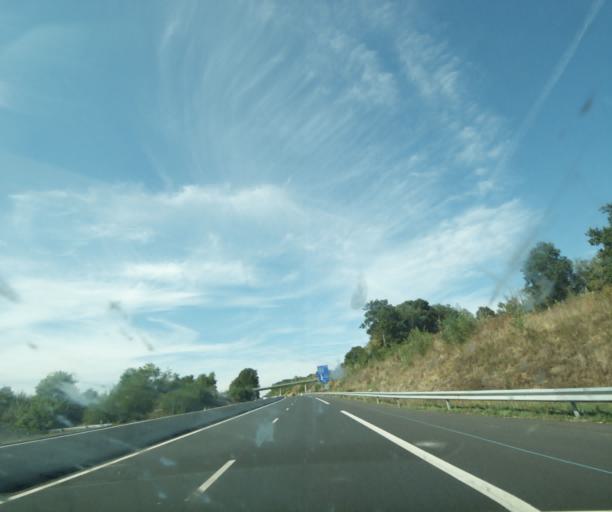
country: FR
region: Limousin
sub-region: Departement de la Correze
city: Saint-Mexant
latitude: 45.3018
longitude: 1.5881
